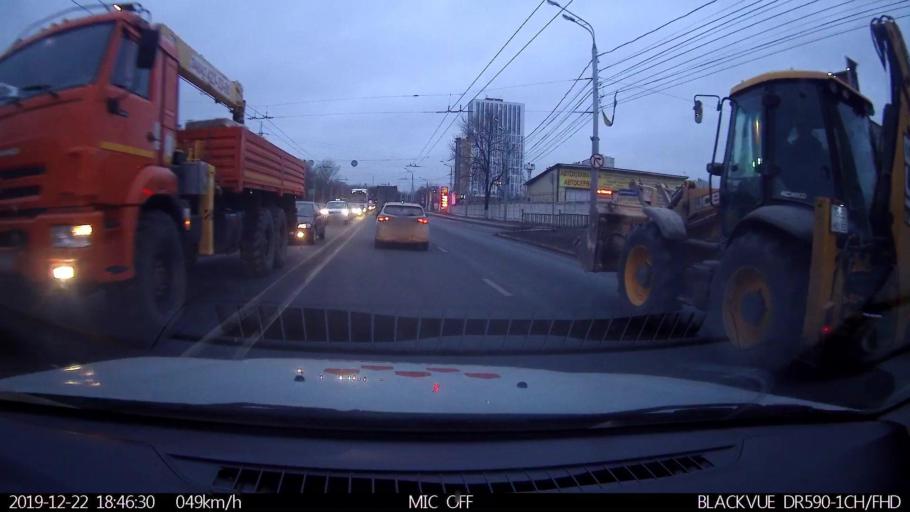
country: RU
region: Nizjnij Novgorod
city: Neklyudovo
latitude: 56.3427
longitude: 43.8764
